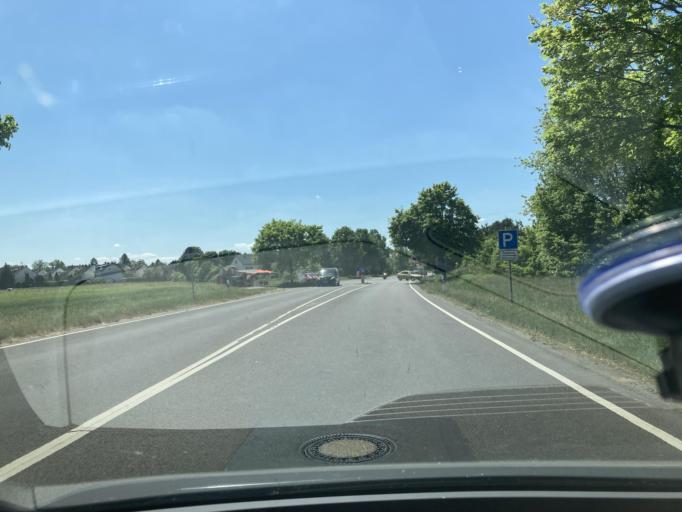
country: DE
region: Hesse
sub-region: Regierungsbezirk Darmstadt
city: Rodgau
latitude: 50.0077
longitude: 8.8744
